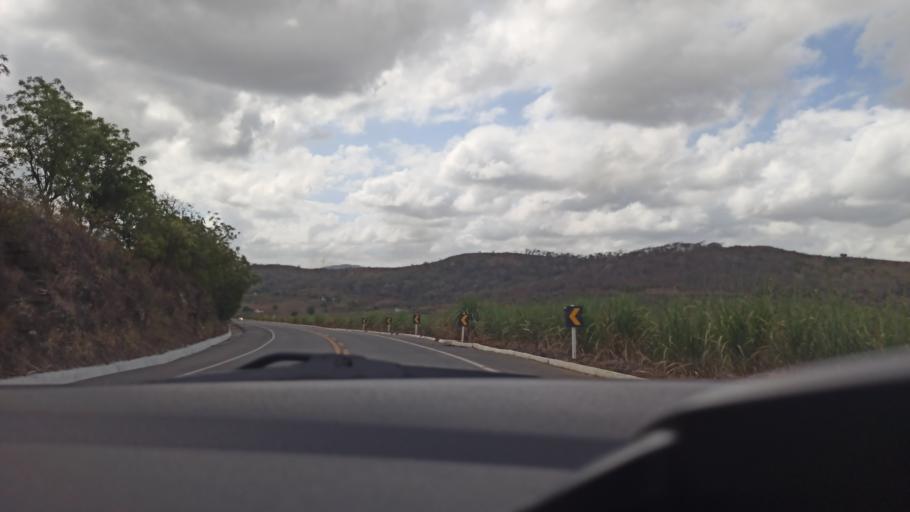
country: BR
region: Pernambuco
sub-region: Timbauba
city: Timbauba
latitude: -7.5354
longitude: -35.2880
